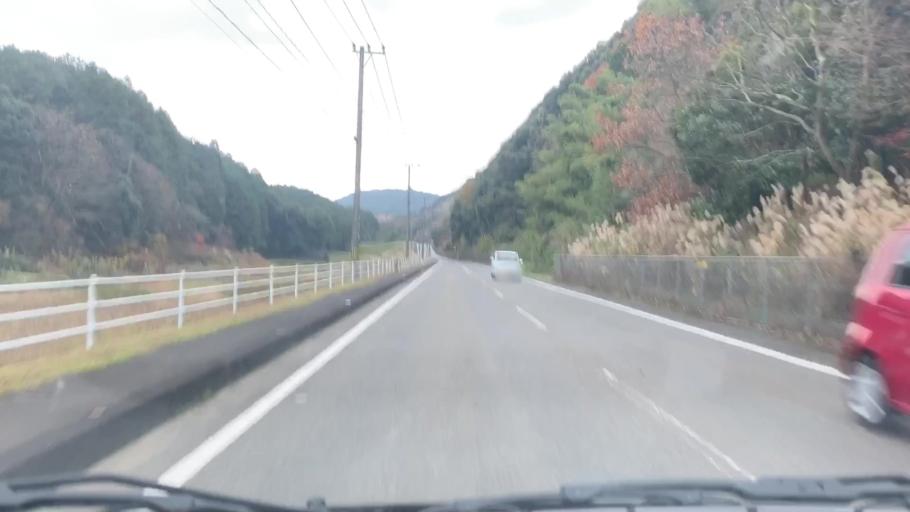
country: JP
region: Saga Prefecture
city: Ureshinomachi-shimojuku
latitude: 33.1189
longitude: 129.9780
